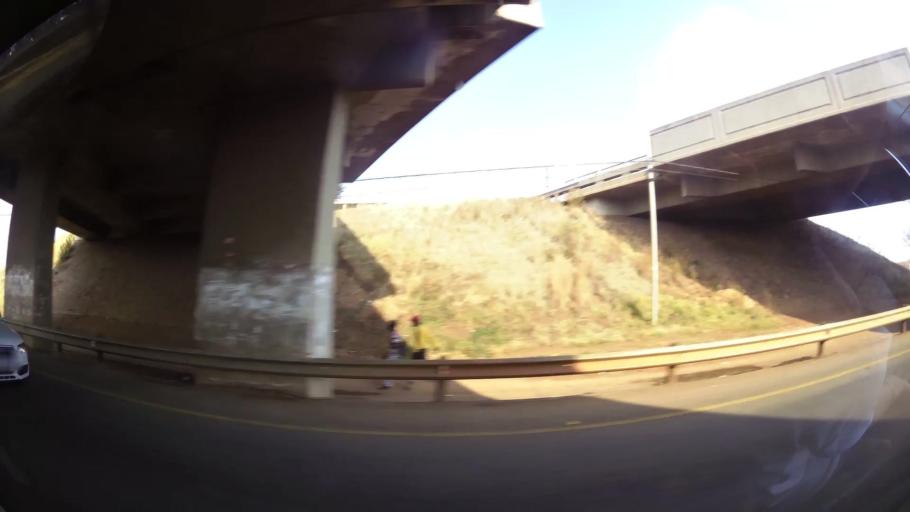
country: ZA
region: Gauteng
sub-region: Ekurhuleni Metropolitan Municipality
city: Germiston
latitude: -26.3412
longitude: 28.2204
